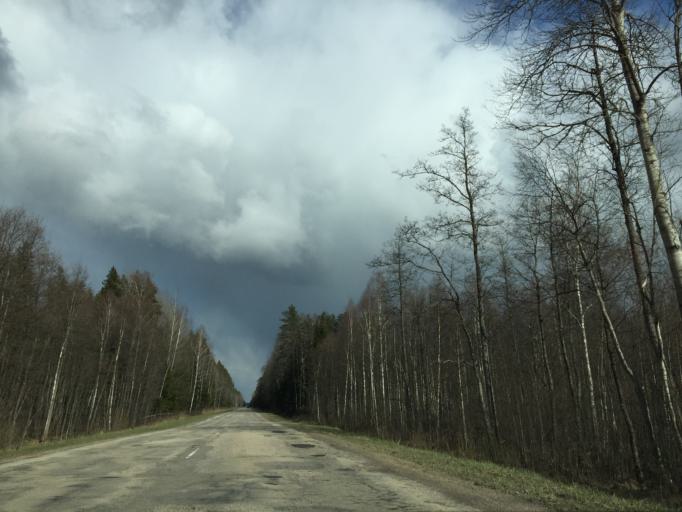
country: LV
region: Garkalne
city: Garkalne
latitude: 56.9462
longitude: 24.4626
